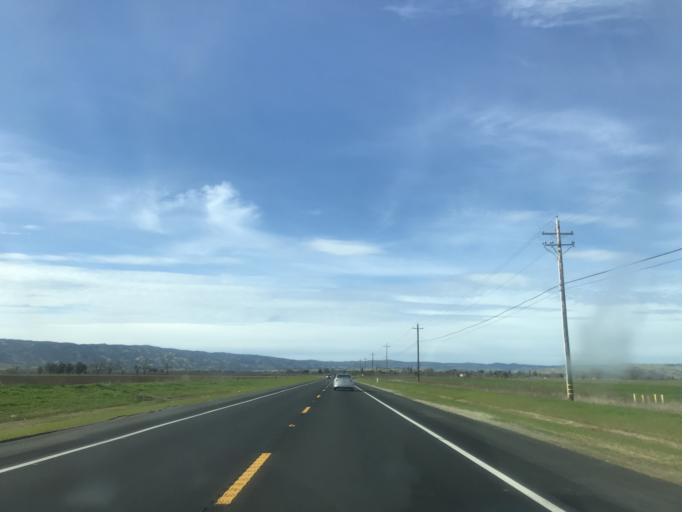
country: US
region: California
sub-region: Yolo County
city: Esparto
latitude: 38.6857
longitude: -121.9940
